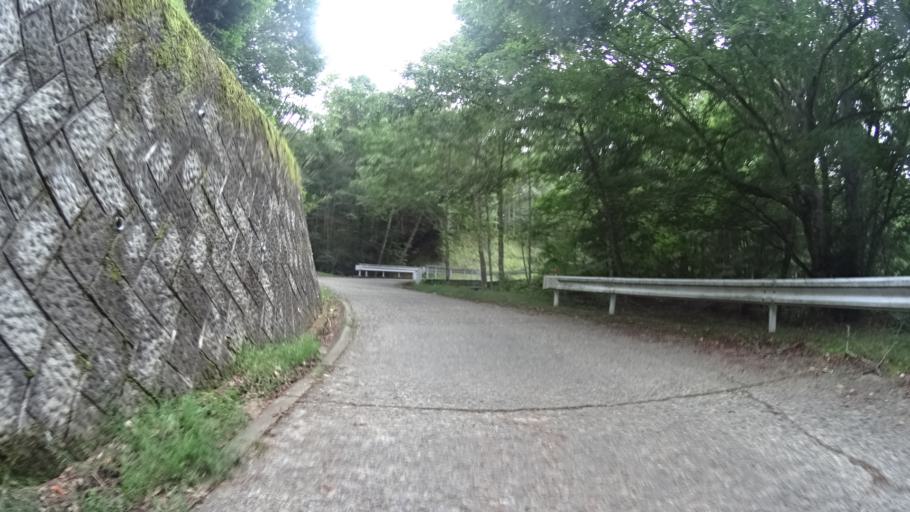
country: JP
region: Yamanashi
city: Kofu-shi
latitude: 35.8534
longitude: 138.5773
